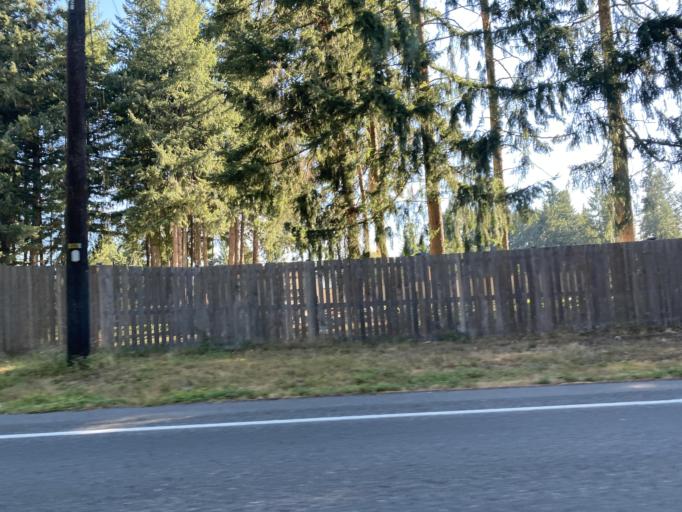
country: US
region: Washington
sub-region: Thurston County
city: Tanglewilde-Thompson Place
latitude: 46.9771
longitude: -122.7620
